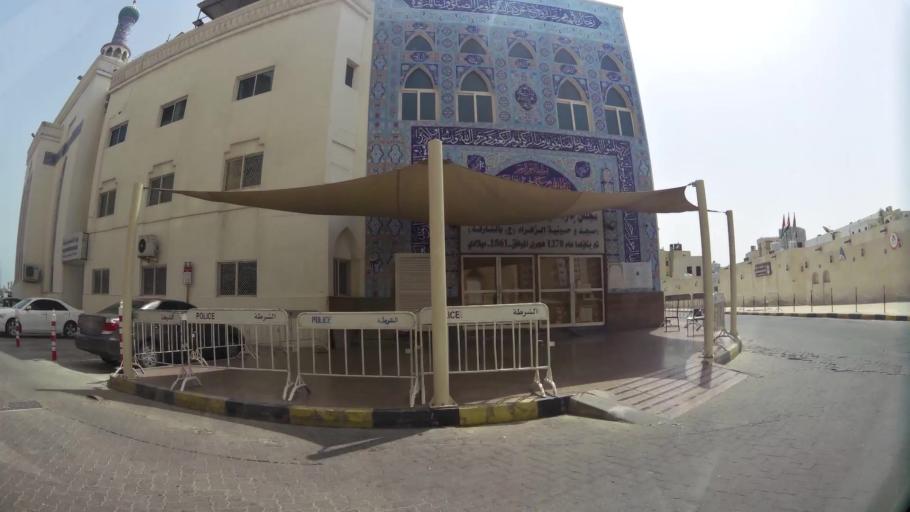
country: AE
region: Ash Shariqah
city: Sharjah
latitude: 25.3576
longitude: 55.3815
